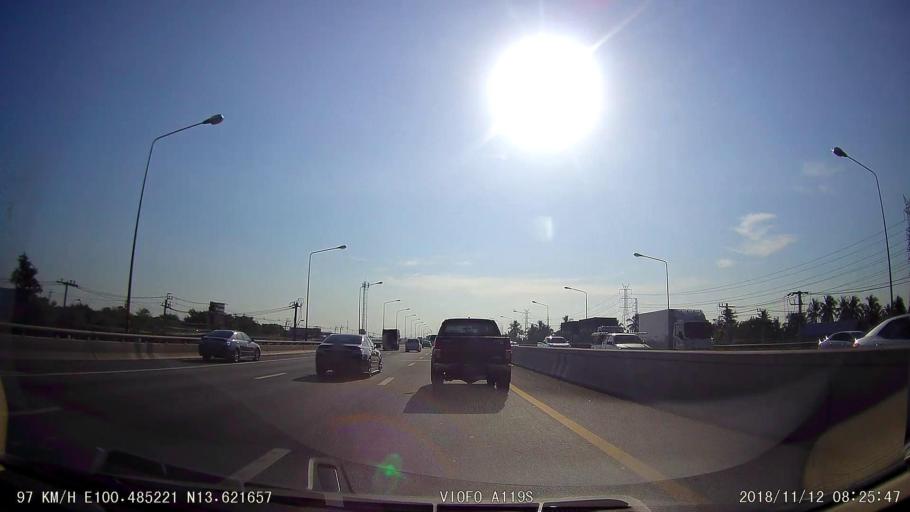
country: TH
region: Bangkok
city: Thung Khru
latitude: 13.6215
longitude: 100.4857
